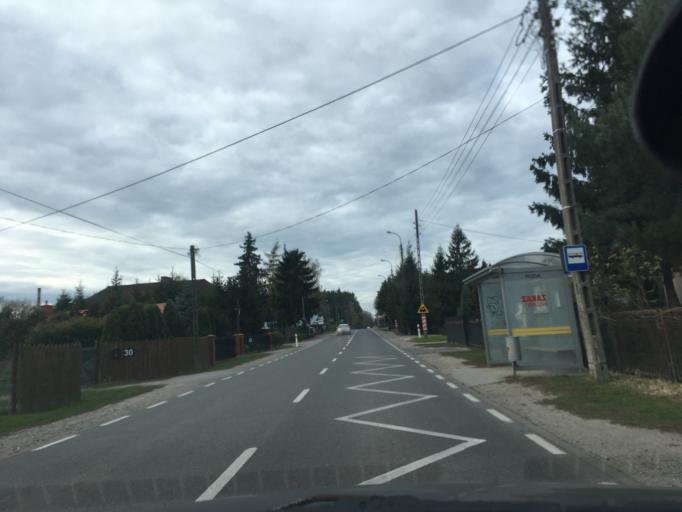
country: PL
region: Masovian Voivodeship
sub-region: Powiat piaseczynski
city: Tarczyn
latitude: 51.9789
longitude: 20.8729
